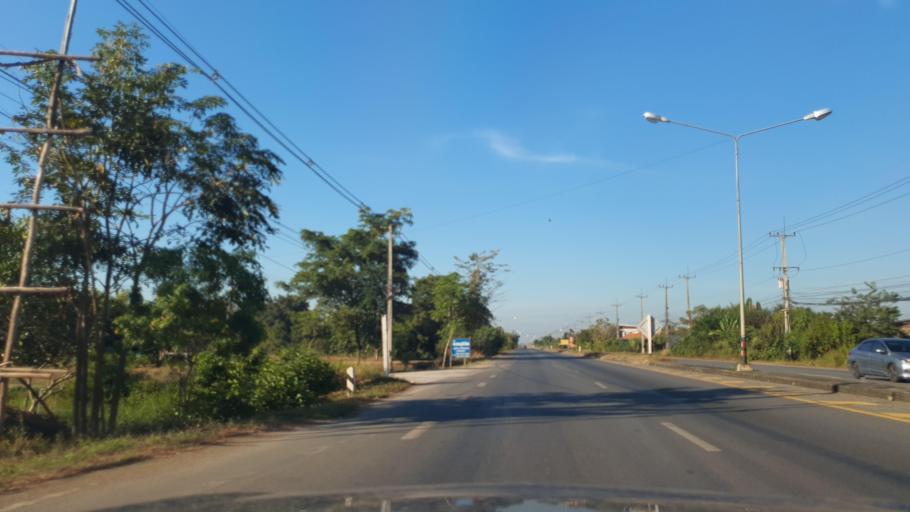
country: TH
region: Sukhothai
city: Kong Krailat
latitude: 16.9646
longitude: 99.9990
